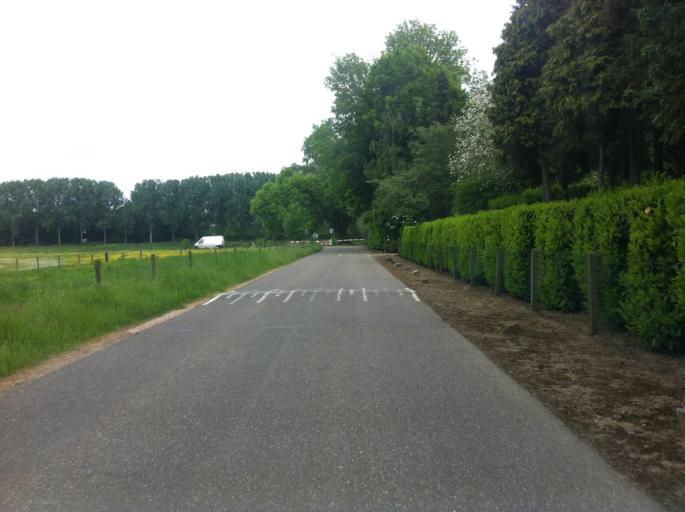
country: NL
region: Limburg
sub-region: Gemeente Roermond
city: Roermond
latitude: 51.2089
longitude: 5.9725
